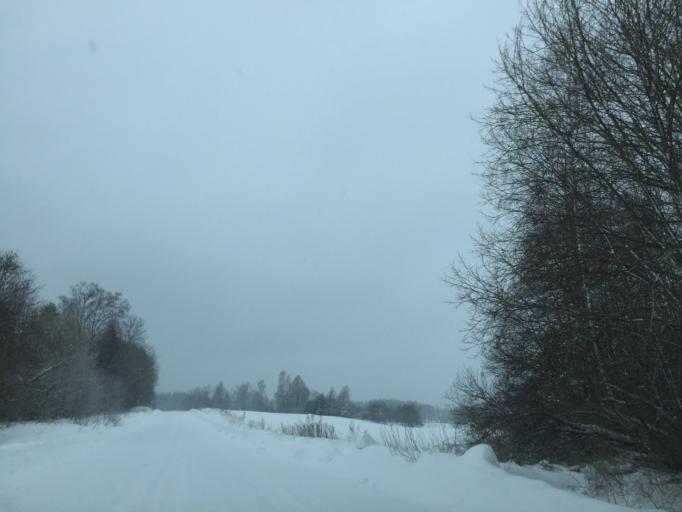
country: LV
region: Amatas Novads
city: Drabesi
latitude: 57.1680
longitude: 25.3079
